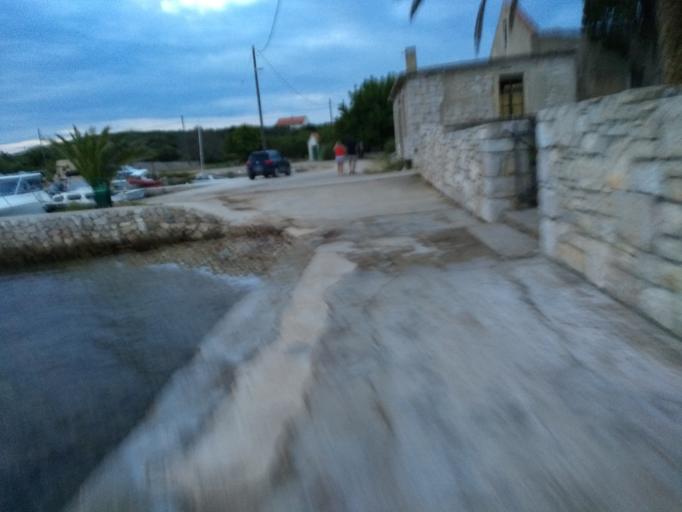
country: HR
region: Zadarska
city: Ugljan
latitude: 44.1385
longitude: 15.0723
